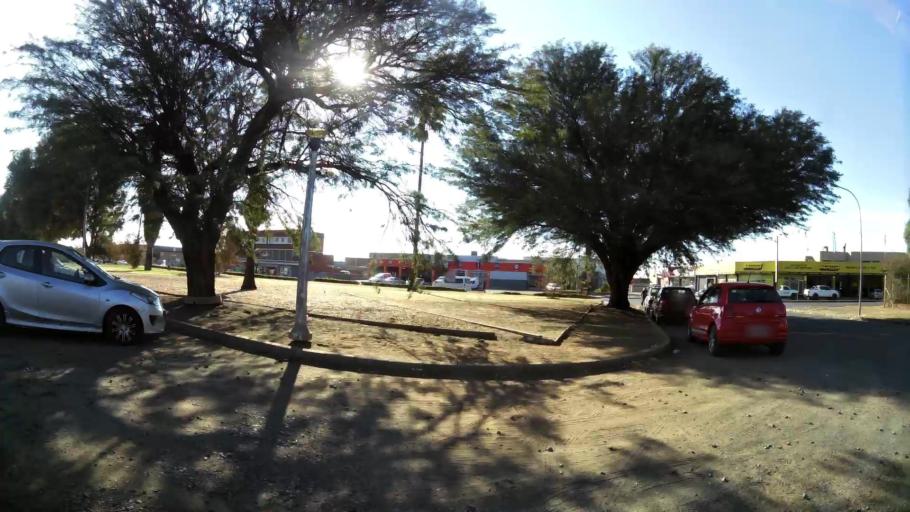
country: ZA
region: Northern Cape
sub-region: Frances Baard District Municipality
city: Kimberley
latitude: -28.7443
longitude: 24.7594
